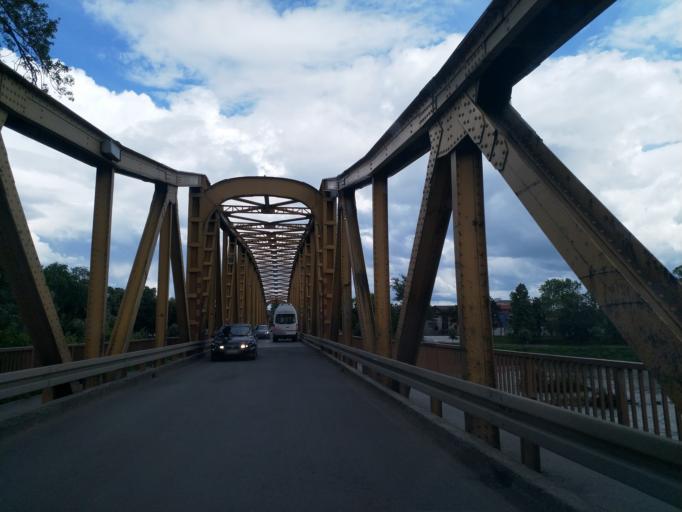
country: RS
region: Central Serbia
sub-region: Pomoravski Okrug
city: Cuprija
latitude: 43.9380
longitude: 21.3679
